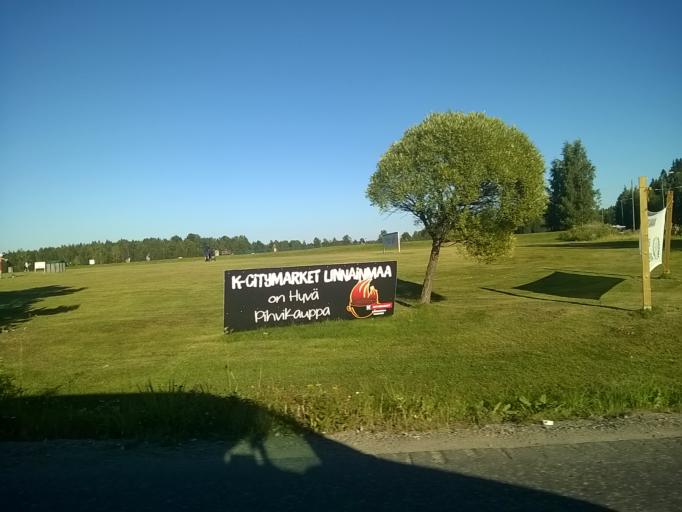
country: FI
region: Pirkanmaa
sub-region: Tampere
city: Tampere
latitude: 61.5057
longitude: 23.8452
